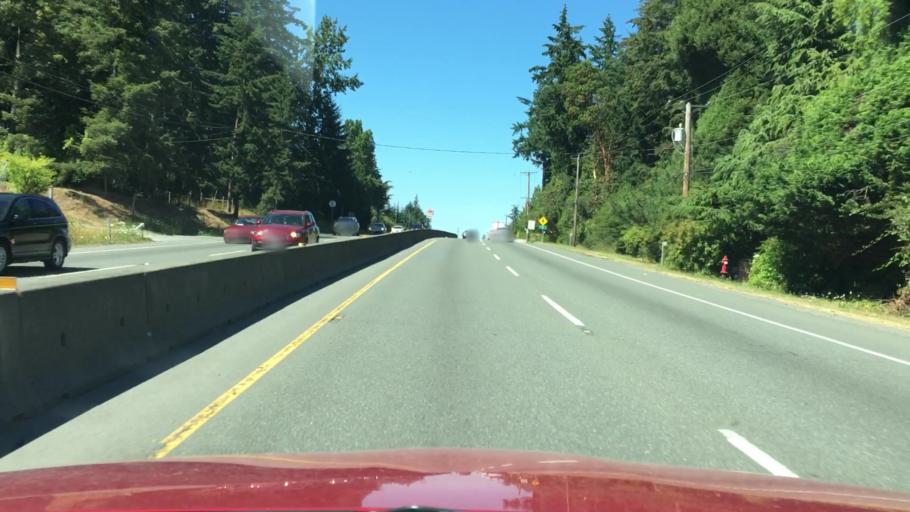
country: CA
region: British Columbia
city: Victoria
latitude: 48.5496
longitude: -123.3920
